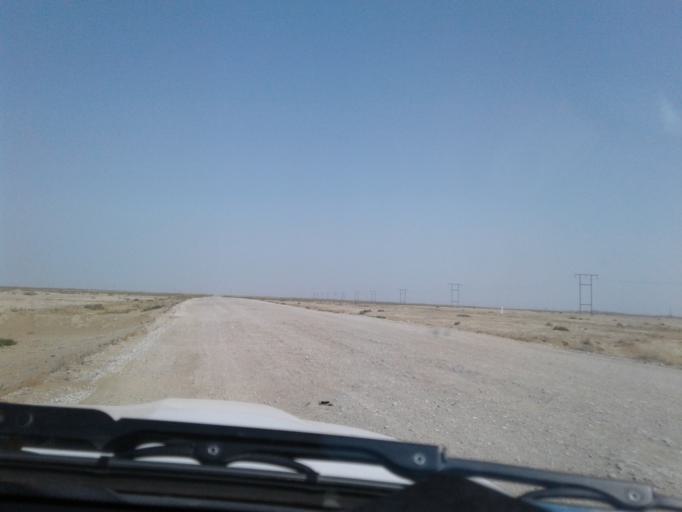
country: IR
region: Golestan
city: Gomishan
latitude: 37.8771
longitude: 53.8743
